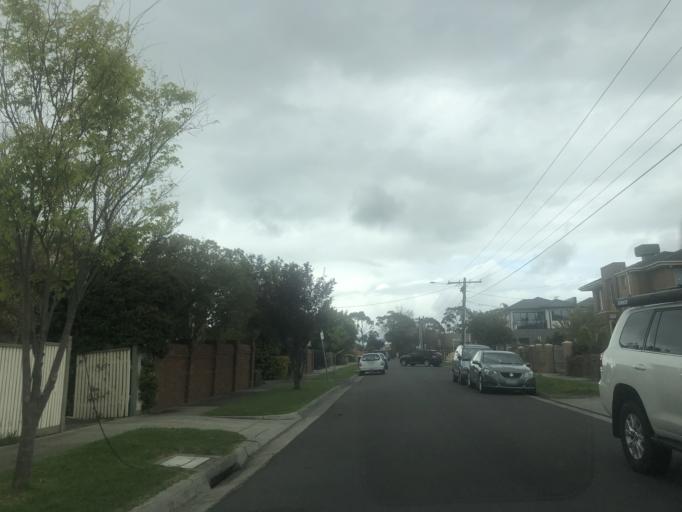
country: AU
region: Victoria
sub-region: Greater Dandenong
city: Dandenong
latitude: -37.9789
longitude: 145.2114
